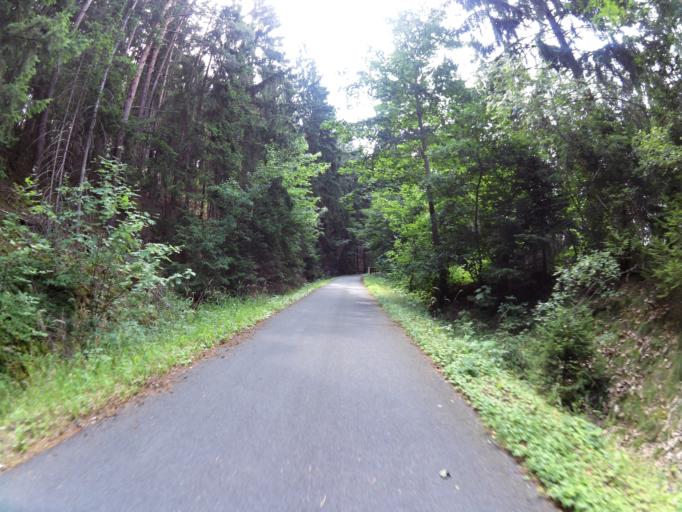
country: DE
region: Thuringia
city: Gorkwitz
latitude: 50.5646
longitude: 11.7635
